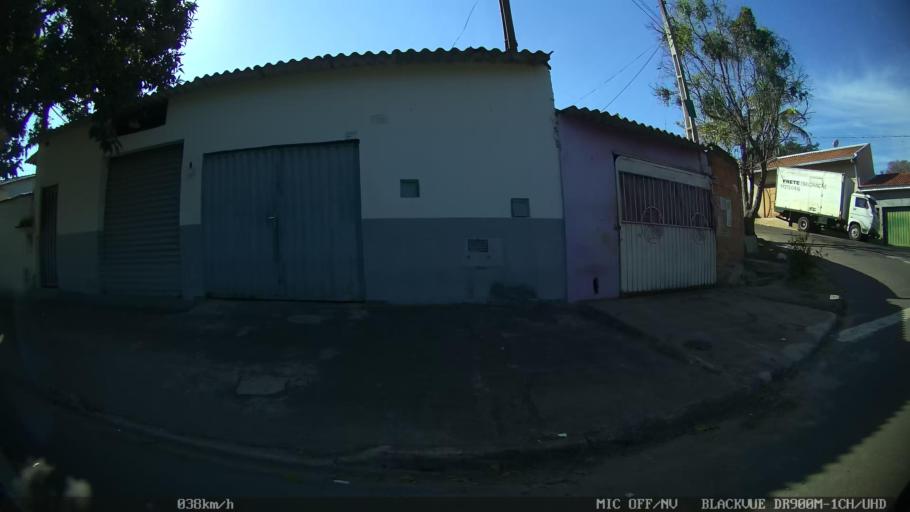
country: BR
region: Sao Paulo
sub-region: Franca
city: Franca
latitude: -20.4913
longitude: -47.4201
